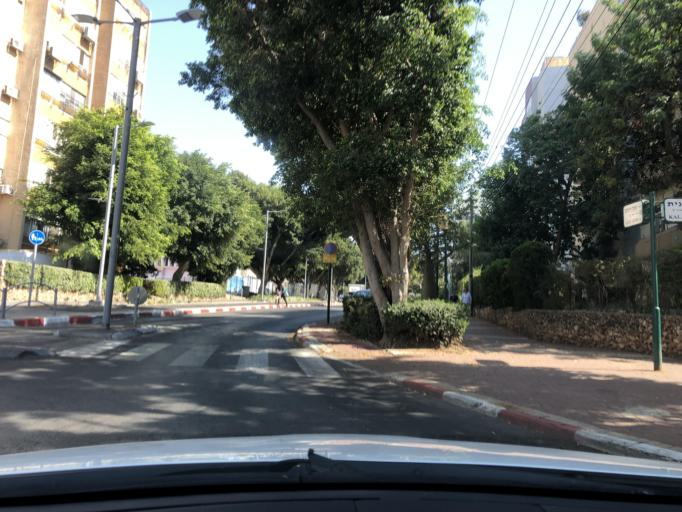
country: IL
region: Central District
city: Kfar Saba
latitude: 32.1759
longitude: 34.8950
